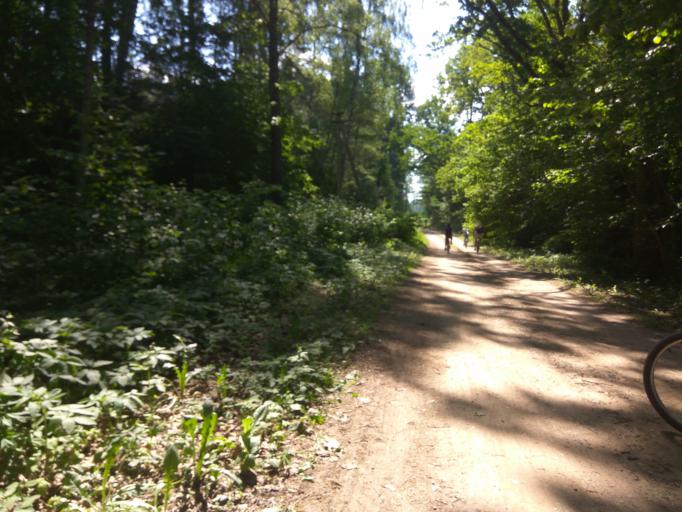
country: LV
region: Kuldigas Rajons
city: Kuldiga
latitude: 56.9375
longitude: 21.9739
